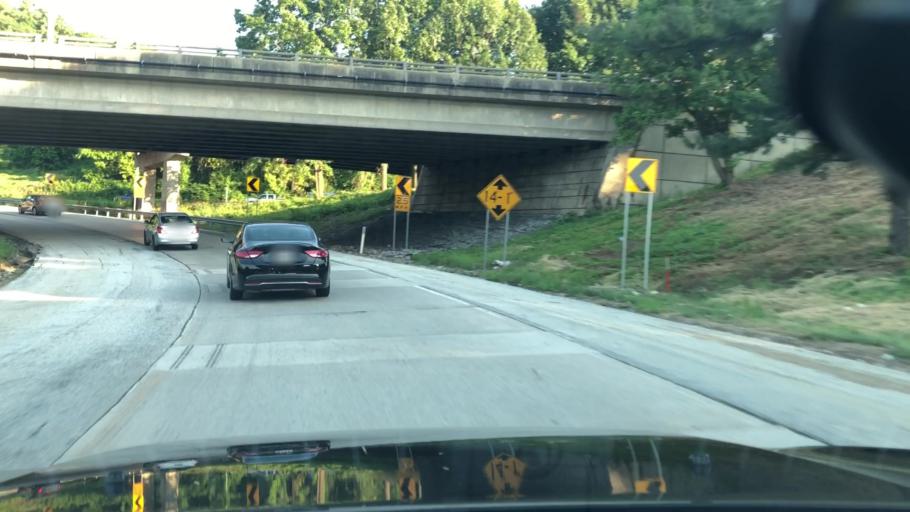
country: US
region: Pennsylvania
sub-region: Montgomery County
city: West Conshohocken
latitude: 40.0649
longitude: -75.3238
